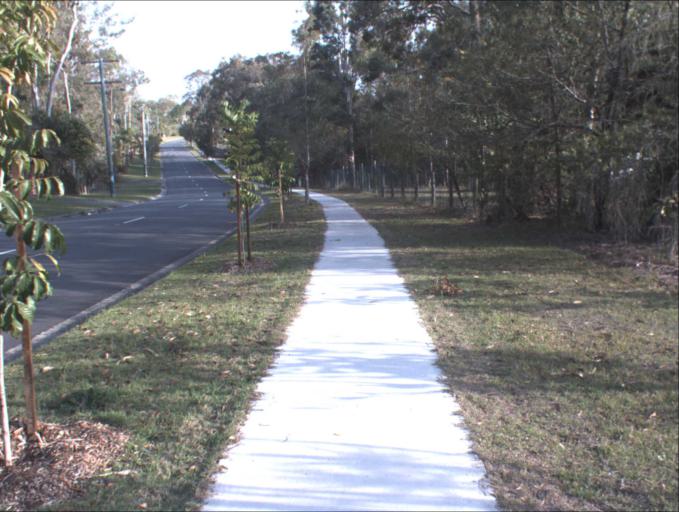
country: AU
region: Queensland
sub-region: Logan
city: Park Ridge South
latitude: -27.6718
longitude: 153.0134
